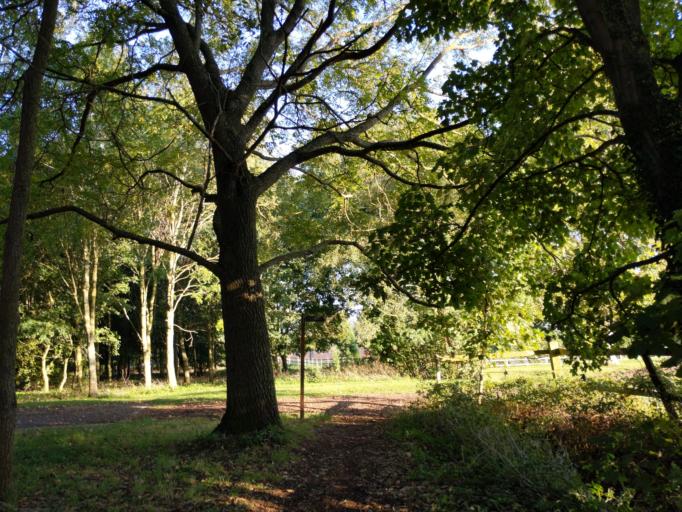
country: GB
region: England
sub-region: Oxfordshire
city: Radley
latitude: 51.6954
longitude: -1.2461
